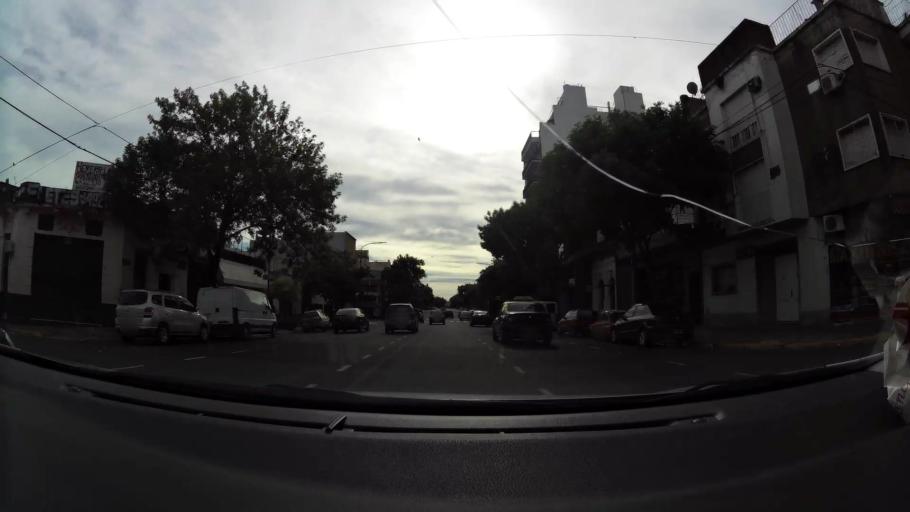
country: AR
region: Buenos Aires F.D.
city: Buenos Aires
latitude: -34.6317
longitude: -58.4184
